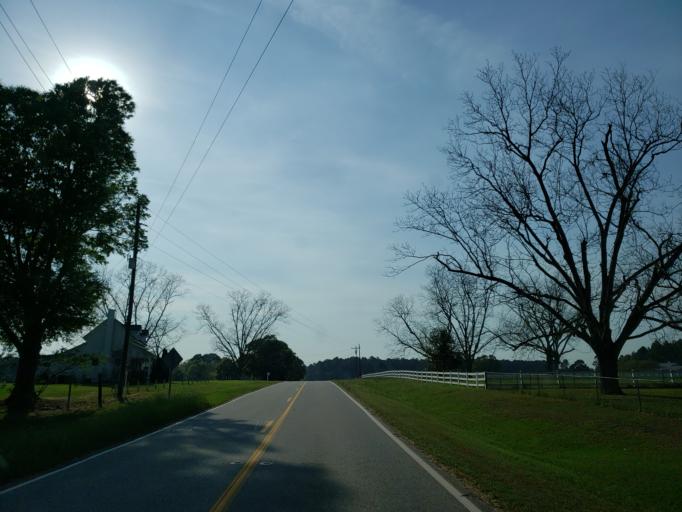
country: US
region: Georgia
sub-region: Tift County
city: Tifton
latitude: 31.5578
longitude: -83.4910
